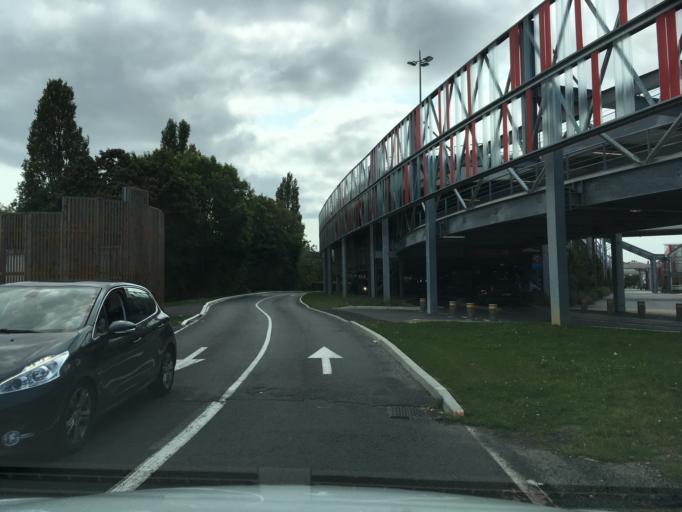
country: FR
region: Aquitaine
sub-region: Departement des Pyrenees-Atlantiques
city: Bayonne
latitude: 43.4894
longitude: -1.4962
